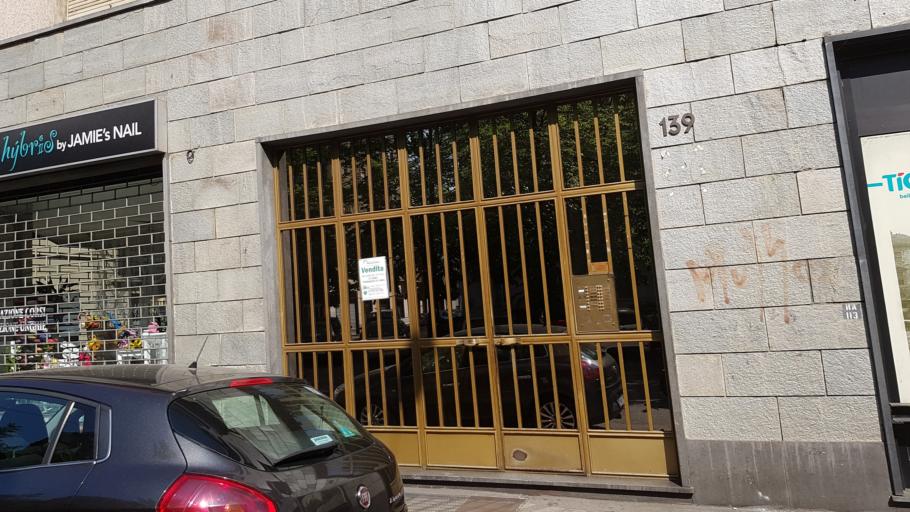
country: IT
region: Piedmont
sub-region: Provincia di Torino
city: Lesna
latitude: 45.0619
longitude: 7.6453
